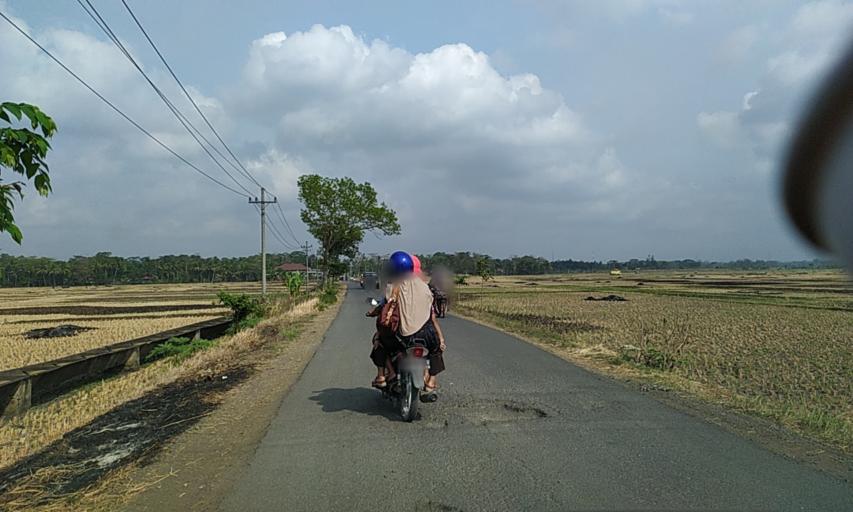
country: ID
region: Central Java
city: Kedungwringin
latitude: -7.4794
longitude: 108.7623
